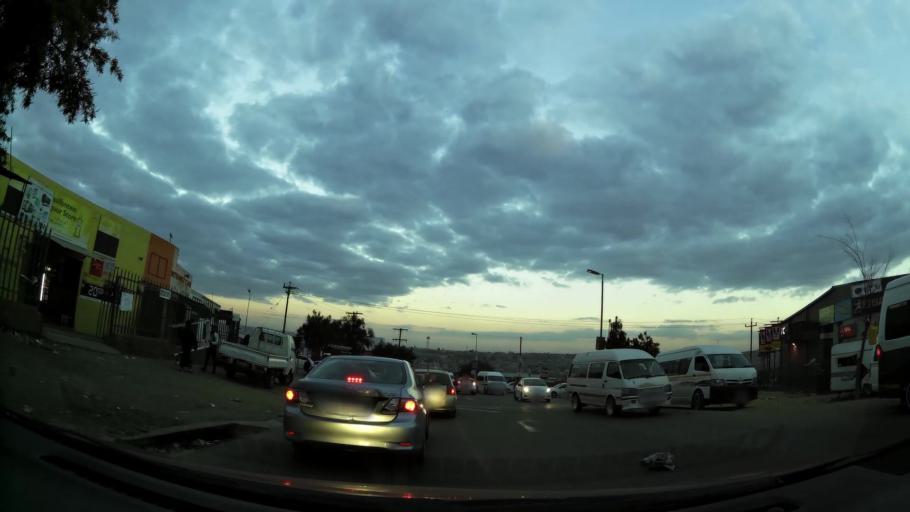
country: ZA
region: Gauteng
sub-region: City of Johannesburg Metropolitan Municipality
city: Midrand
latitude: -25.9886
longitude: 28.1740
